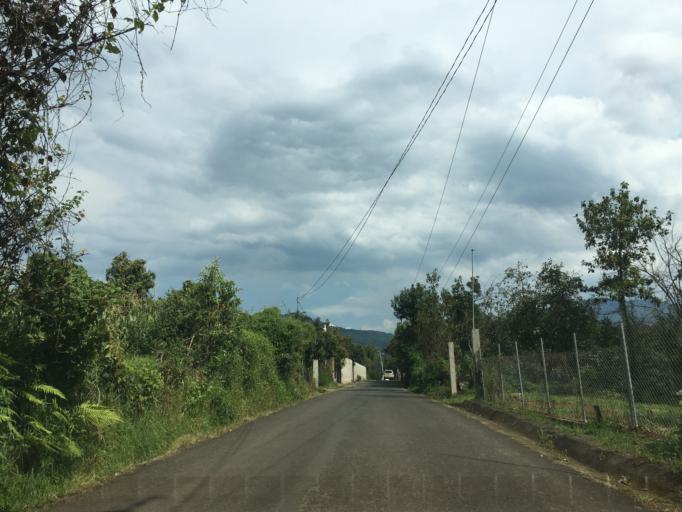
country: MX
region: Michoacan
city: Tingambato
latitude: 19.4999
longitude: -101.8661
